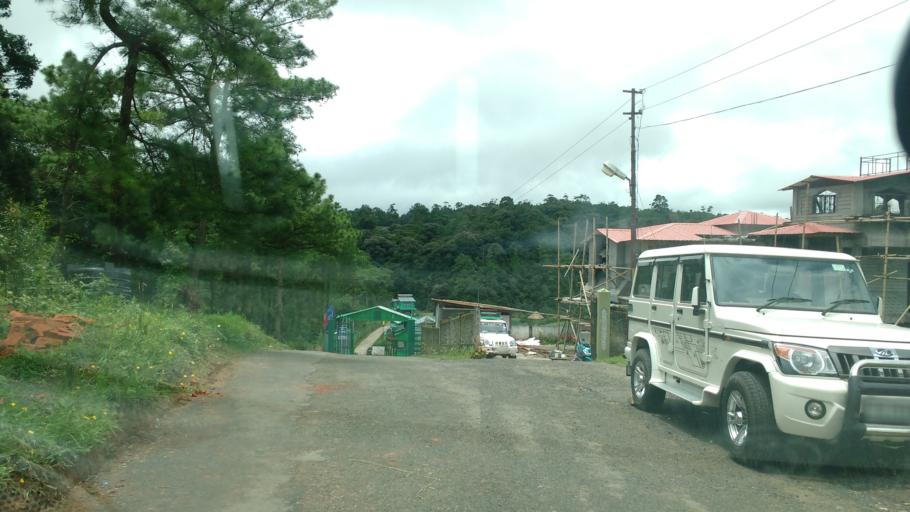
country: IN
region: Meghalaya
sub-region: East Khasi Hills
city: Shillong
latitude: 25.5407
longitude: 91.8214
